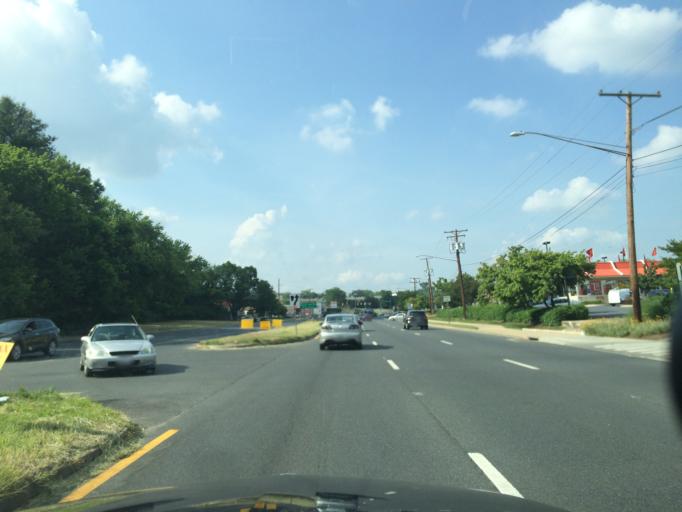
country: US
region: Maryland
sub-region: Montgomery County
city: Aspen Hill
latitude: 39.0778
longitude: -77.0808
